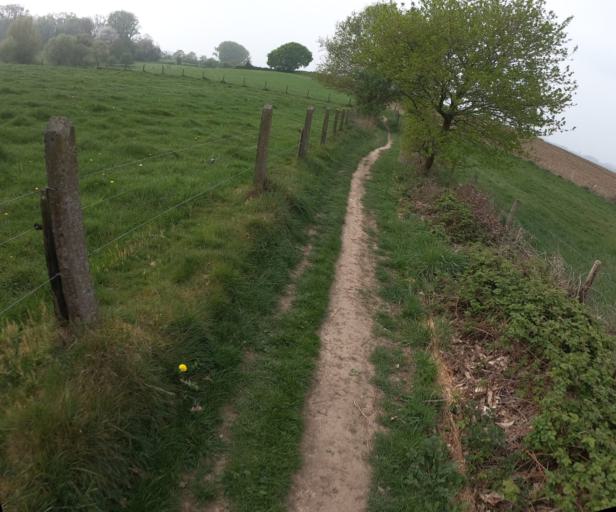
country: BE
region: Flanders
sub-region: Provincie Vlaams-Brabant
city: Gooik
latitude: 50.7817
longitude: 4.1066
